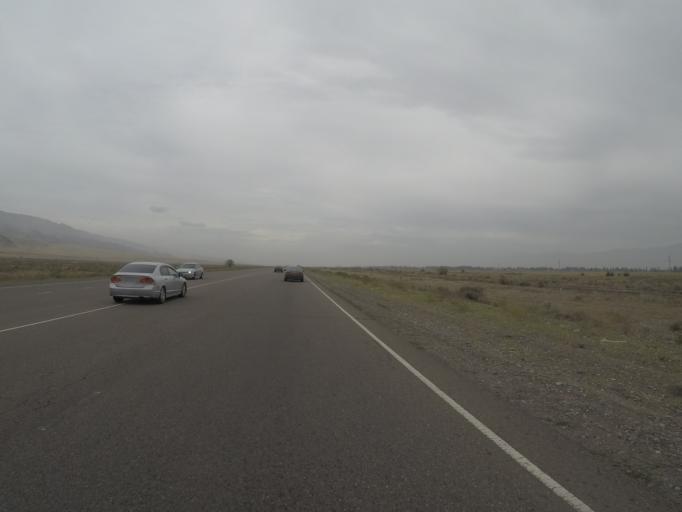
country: KG
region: Chuy
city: Tokmok
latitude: 42.8298
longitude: 75.4923
